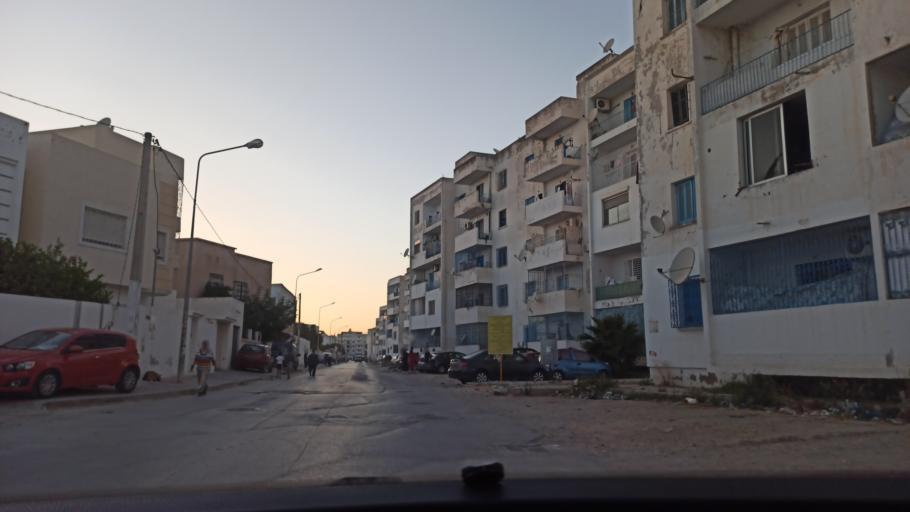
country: TN
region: Ariana
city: Ariana
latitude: 36.8655
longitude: 10.1979
